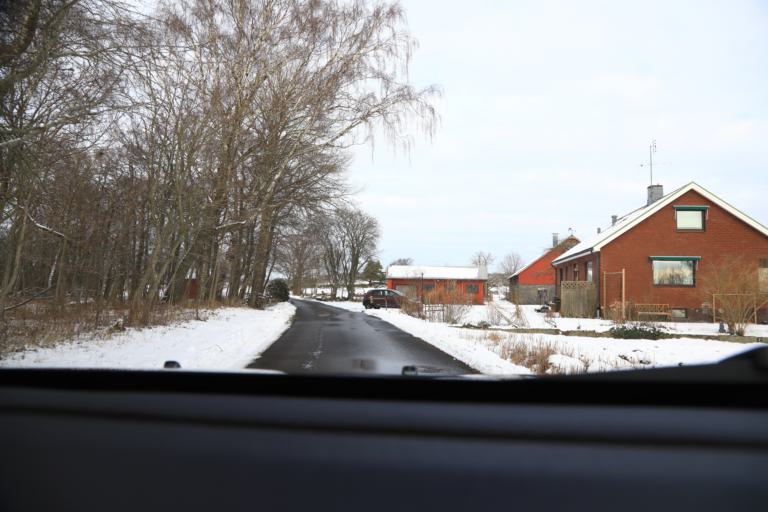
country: SE
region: Halland
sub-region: Kungsbacka Kommun
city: Frillesas
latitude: 57.2308
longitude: 12.1906
